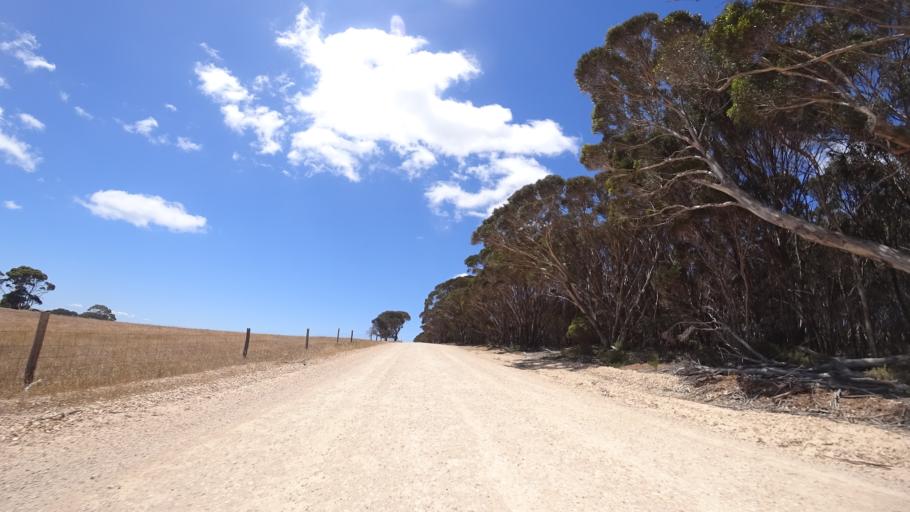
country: AU
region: South Australia
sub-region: Kangaroo Island
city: Kingscote
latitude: -35.8222
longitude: 138.0421
